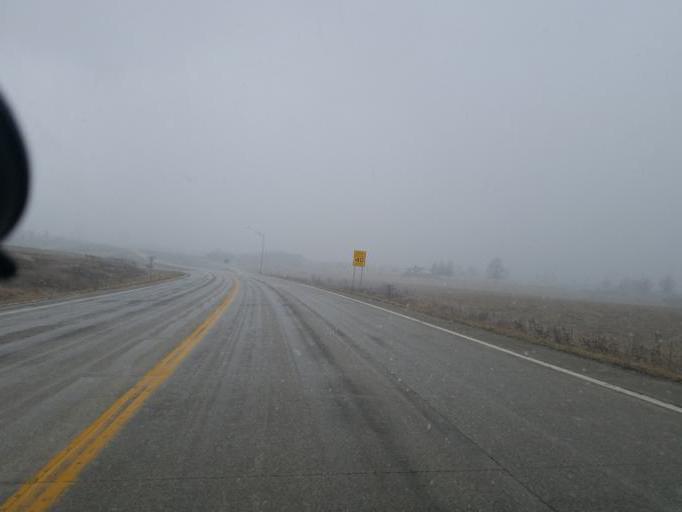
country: US
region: Missouri
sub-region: Adair County
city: Kirksville
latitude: 40.2424
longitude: -92.5817
